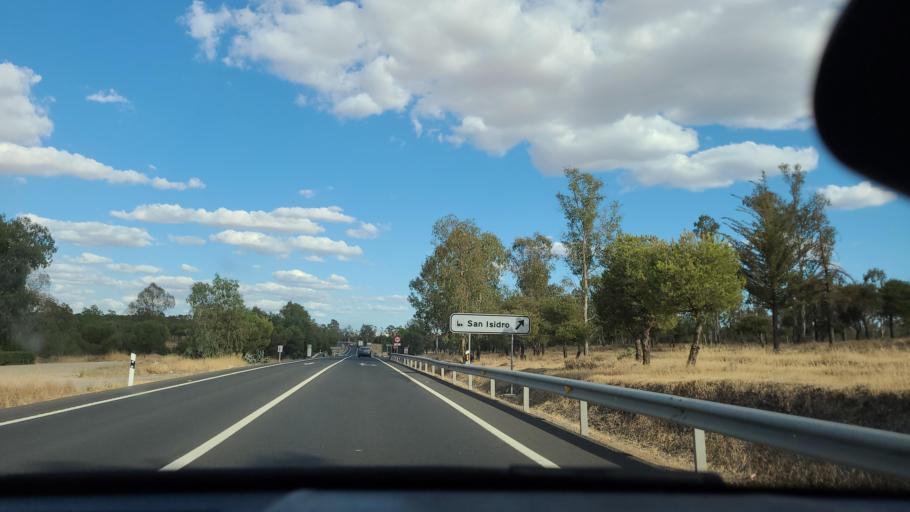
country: ES
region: Extremadura
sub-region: Provincia de Badajoz
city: Berlanga
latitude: 38.2740
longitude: -5.8173
